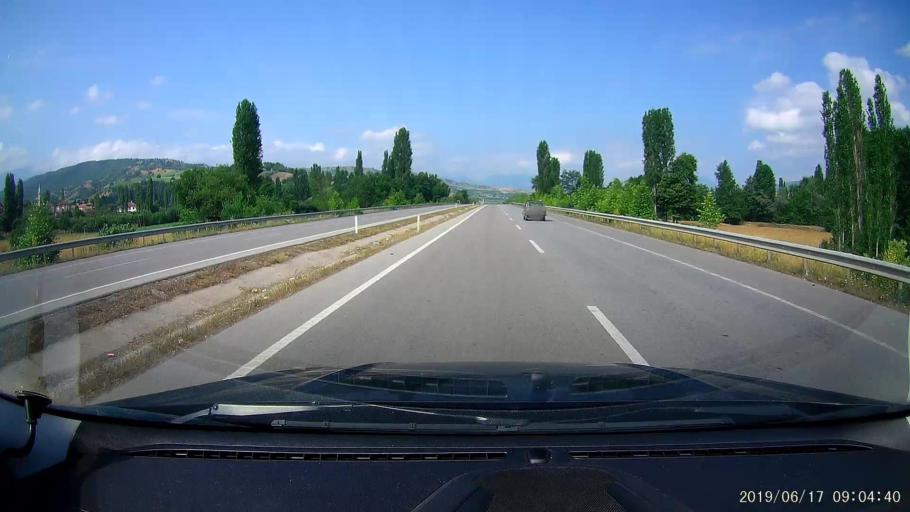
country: TR
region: Amasya
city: Tasova
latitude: 40.7434
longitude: 36.2832
